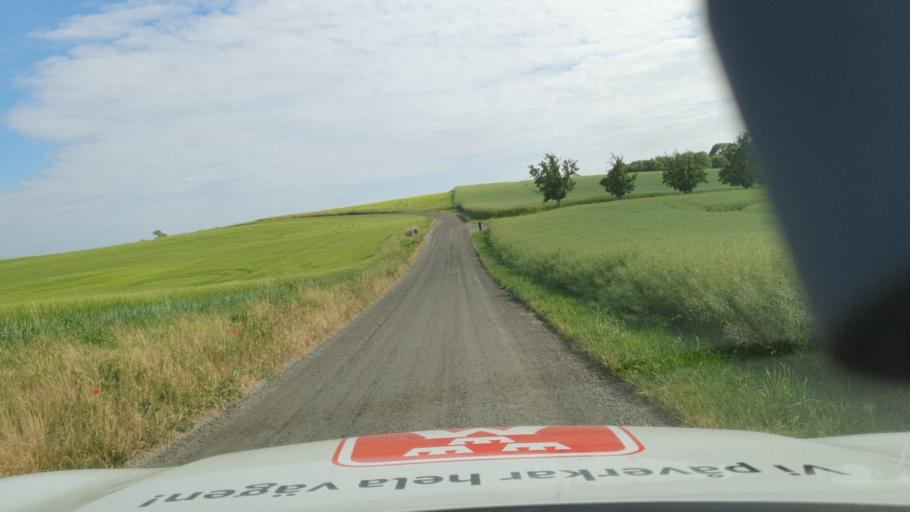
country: SE
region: Skane
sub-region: Skurups Kommun
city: Skivarp
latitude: 55.4348
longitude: 13.5953
